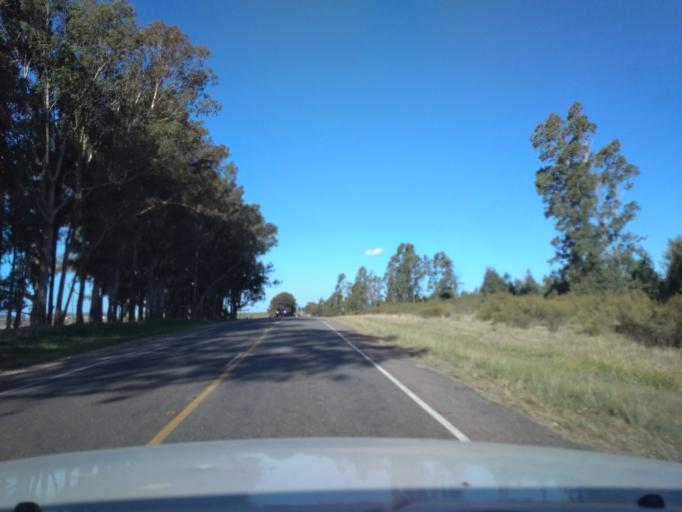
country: UY
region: Florida
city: Casupa
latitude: -34.0398
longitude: -55.9124
